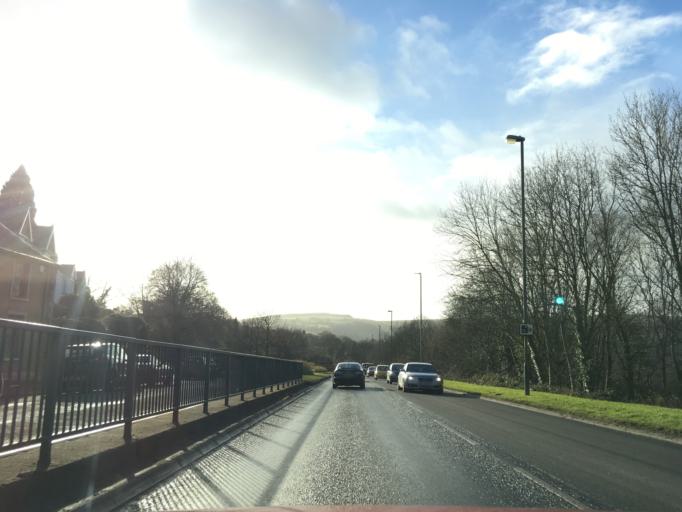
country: GB
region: Wales
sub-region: Caerphilly County Borough
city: Hengoed
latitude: 51.6445
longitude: -3.2230
